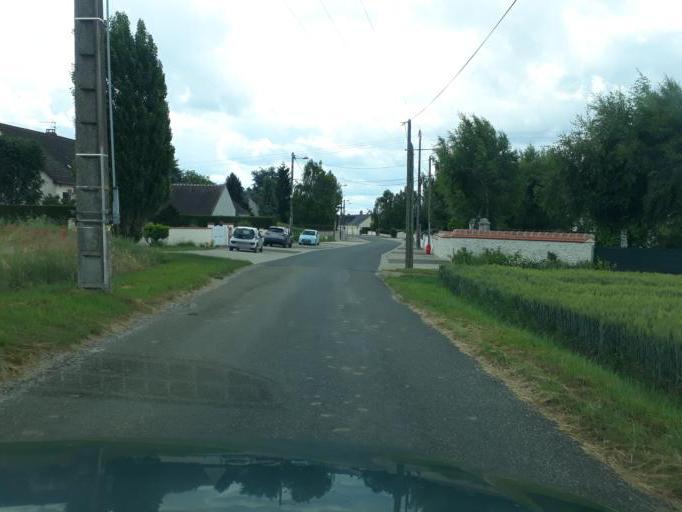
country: FR
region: Centre
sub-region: Departement du Loiret
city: Ingre
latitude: 47.9180
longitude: 1.8080
